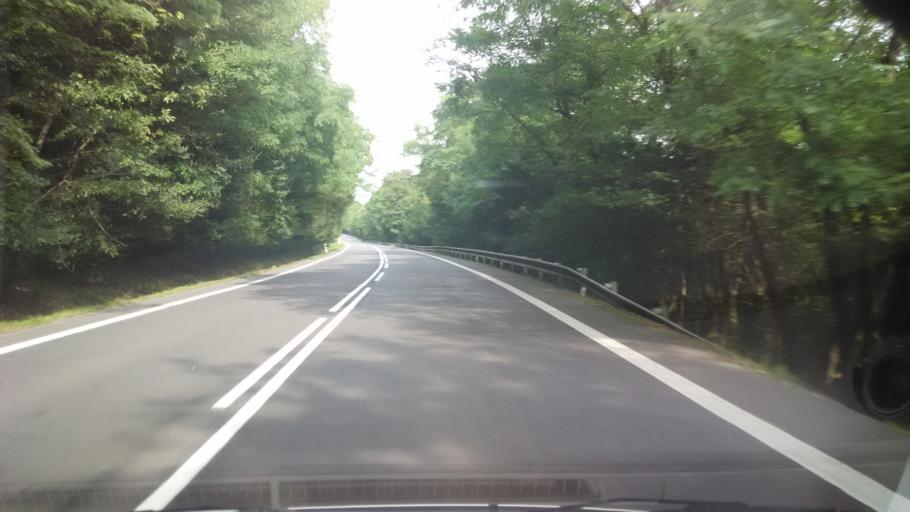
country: SK
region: Banskobystricky
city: Dudince
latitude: 48.2274
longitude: 18.9548
